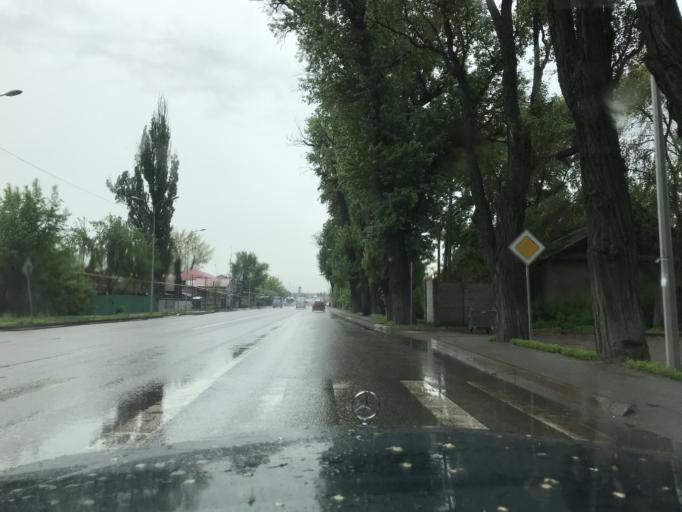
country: KZ
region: Almaty Oblysy
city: Pervomayskiy
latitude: 43.3442
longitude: 76.9675
